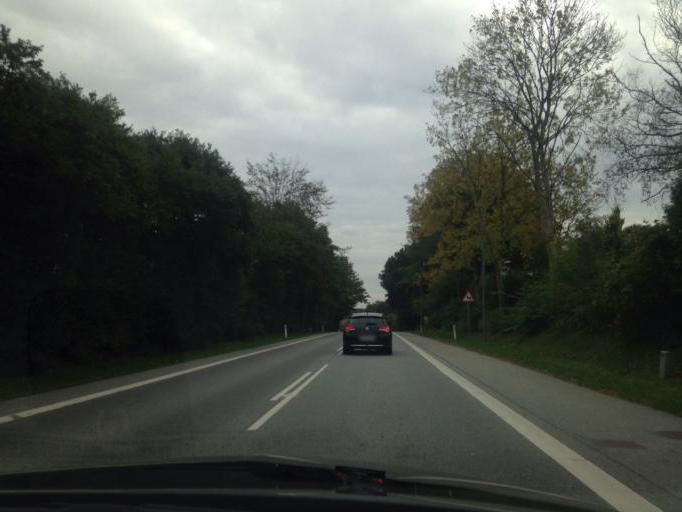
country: DK
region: South Denmark
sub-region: Haderslev Kommune
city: Haderslev
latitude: 55.2449
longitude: 9.4404
